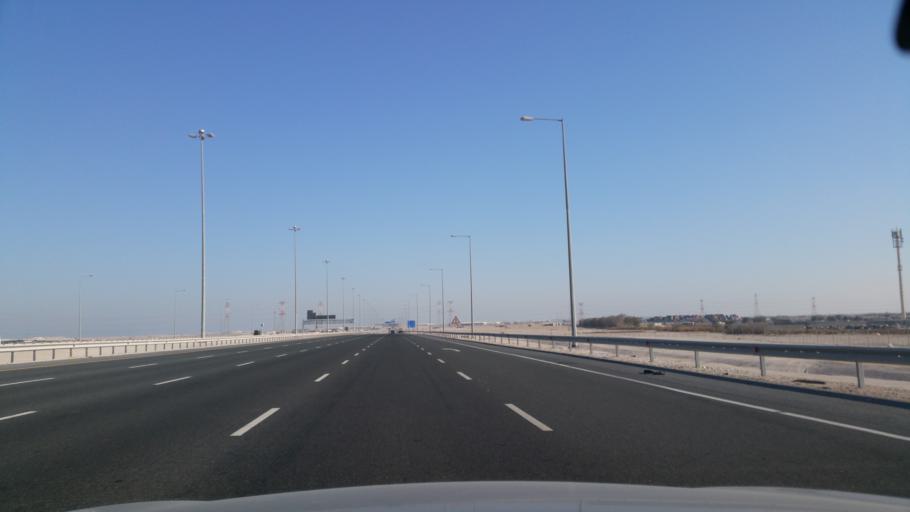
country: QA
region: Al Wakrah
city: Al Wukayr
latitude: 25.1128
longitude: 51.4970
